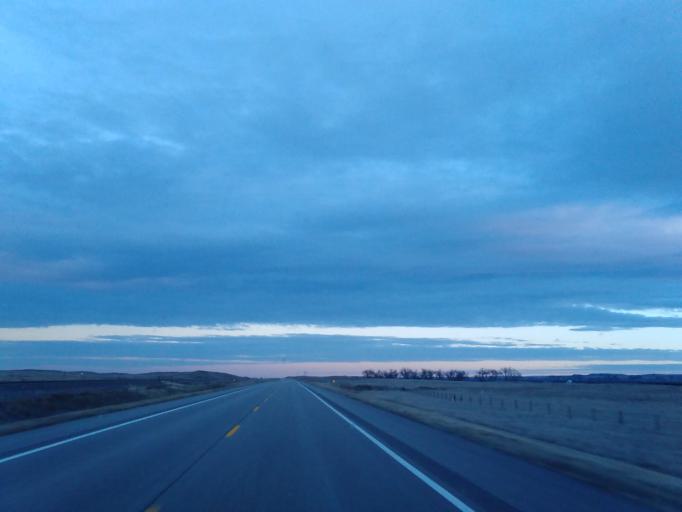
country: US
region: Nebraska
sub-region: Garden County
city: Oshkosh
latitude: 41.3812
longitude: -102.2717
